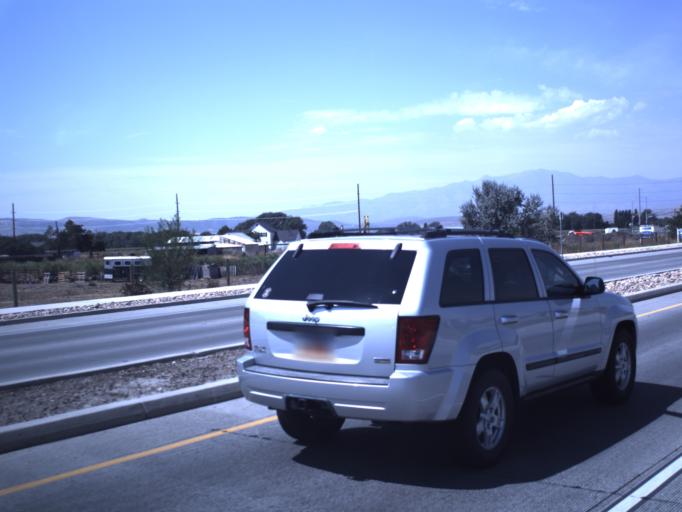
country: US
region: Utah
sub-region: Utah County
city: Lehi
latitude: 40.3748
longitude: -111.8634
